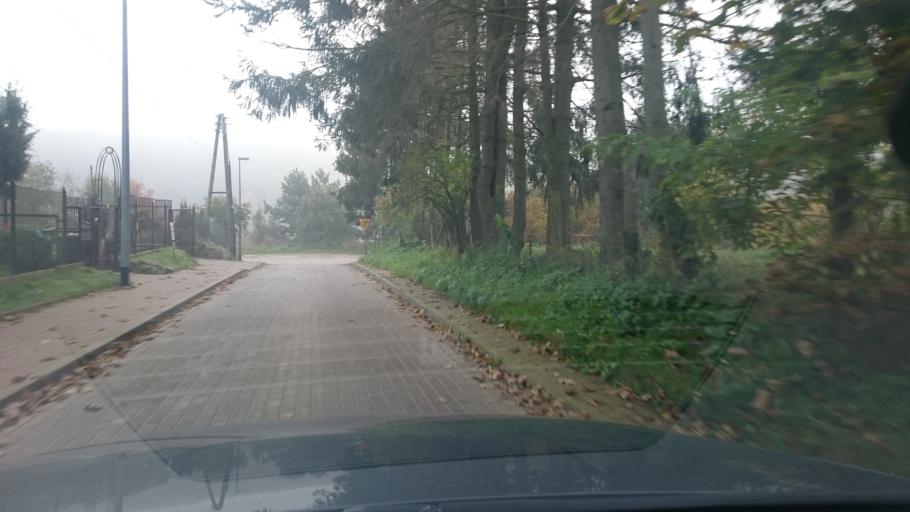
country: PL
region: Pomeranian Voivodeship
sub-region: Gdynia
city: Wielki Kack
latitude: 54.4607
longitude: 18.4941
